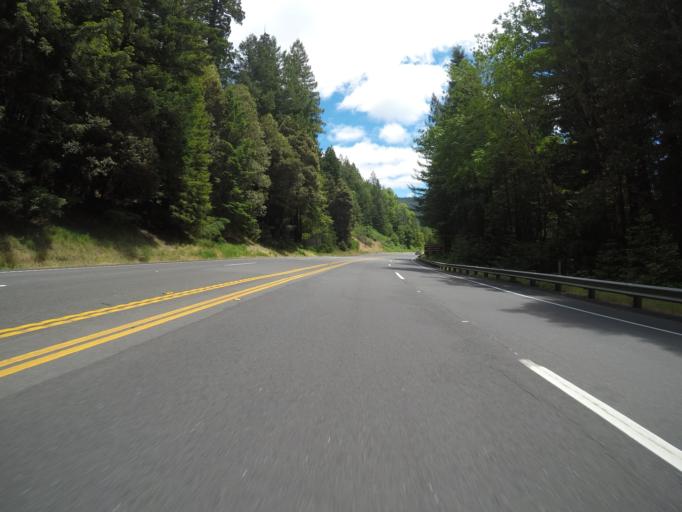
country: US
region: California
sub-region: Humboldt County
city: Redway
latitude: 40.2716
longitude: -123.8758
